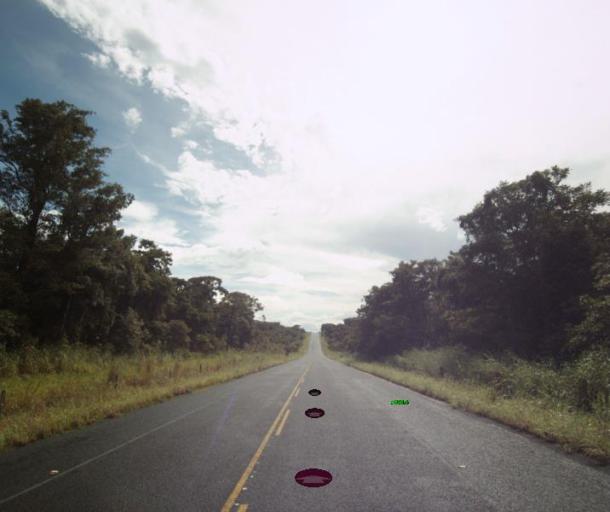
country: BR
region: Goias
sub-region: Sao Miguel Do Araguaia
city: Sao Miguel do Araguaia
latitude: -13.2984
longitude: -50.3257
